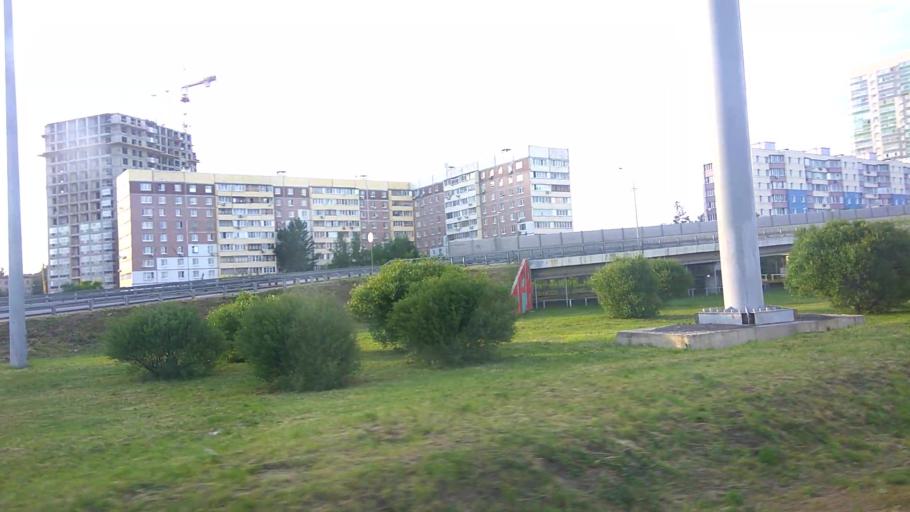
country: RU
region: Moskovskaya
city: Korolev
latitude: 55.9133
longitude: 37.7845
